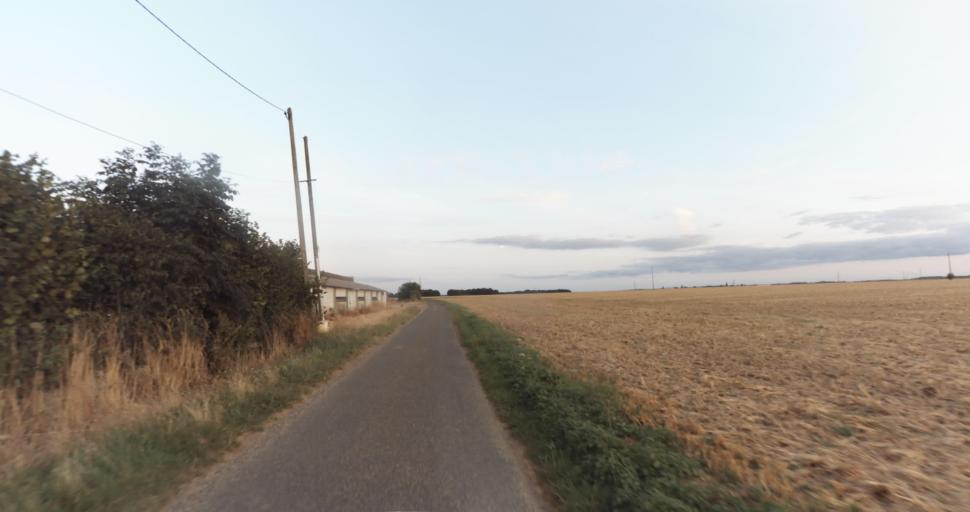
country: FR
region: Haute-Normandie
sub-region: Departement de l'Eure
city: La Madeleine-de-Nonancourt
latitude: 48.8735
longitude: 1.2088
